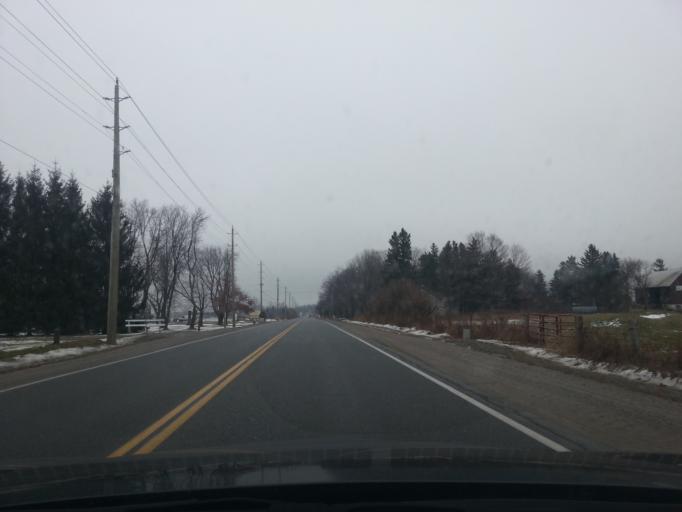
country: CA
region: Ontario
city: Uxbridge
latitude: 44.0872
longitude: -78.9710
